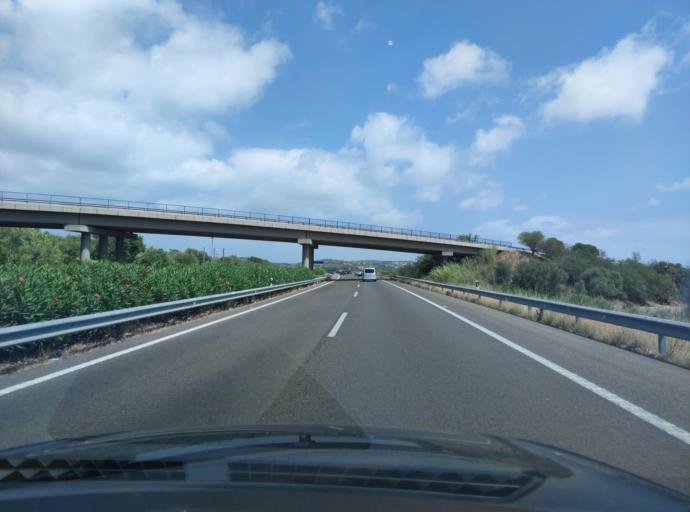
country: ES
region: Valencia
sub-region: Provincia de Castello
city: Vinaros
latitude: 40.4732
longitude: 0.4187
